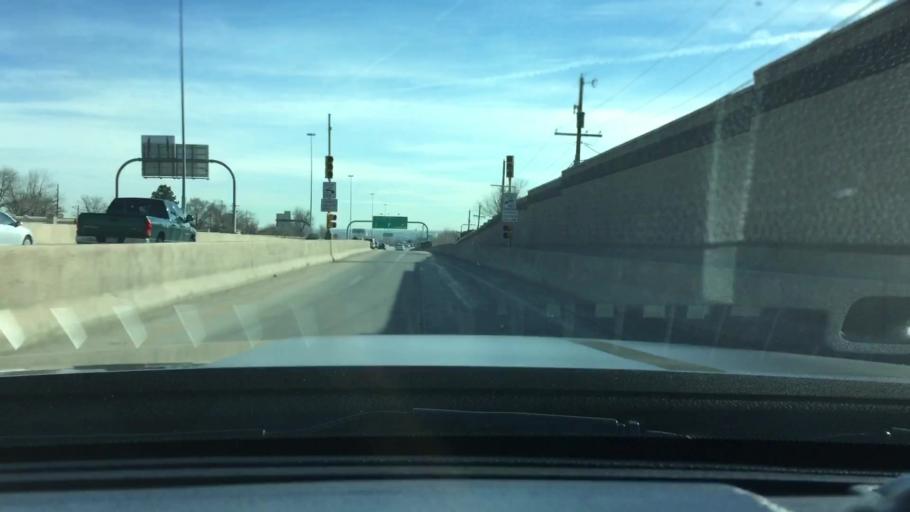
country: US
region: Colorado
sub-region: Adams County
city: Twin Lakes
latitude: 39.8295
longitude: -105.0026
